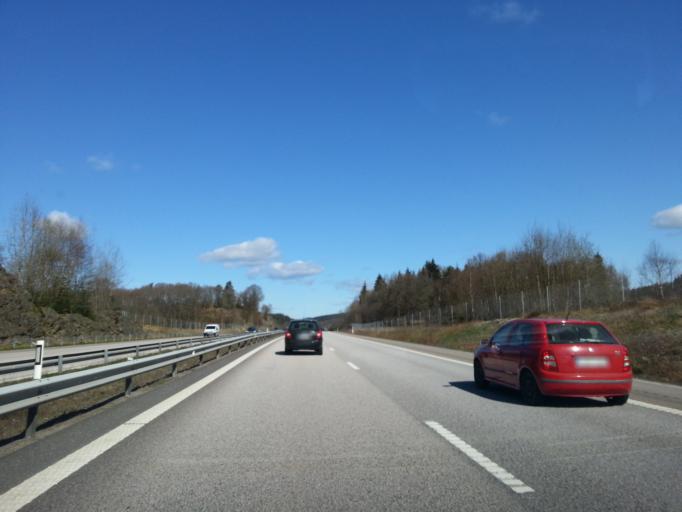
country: SE
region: Vaestra Goetaland
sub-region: Uddevalla Kommun
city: Ljungskile
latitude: 58.2561
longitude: 11.9011
